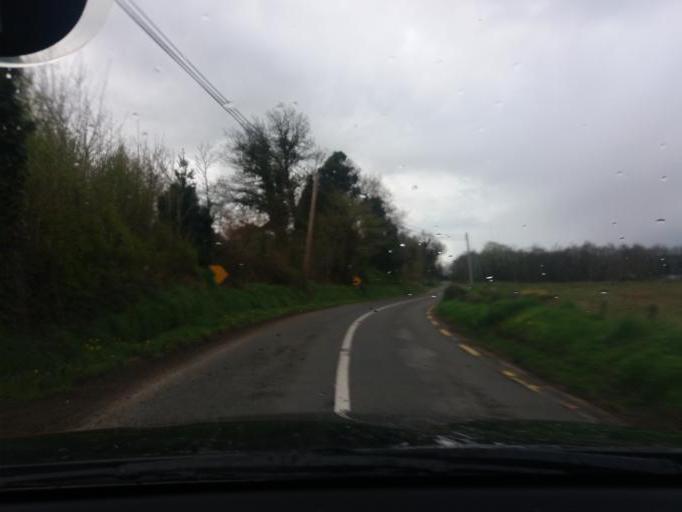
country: IE
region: Ulster
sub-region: An Cabhan
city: Ballyconnell
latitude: 54.1429
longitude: -7.7015
